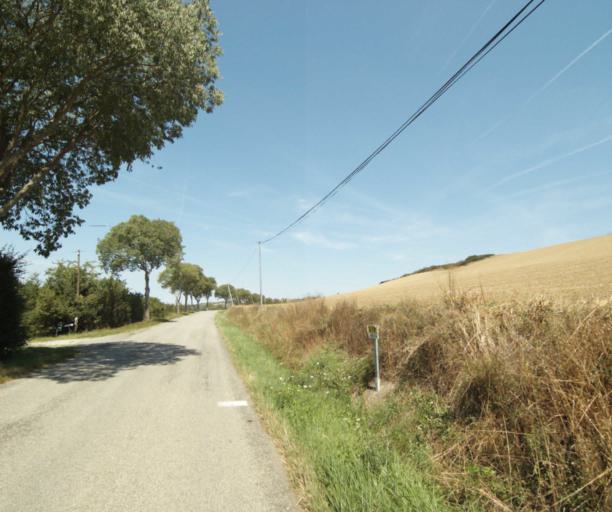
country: FR
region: Midi-Pyrenees
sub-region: Departement de l'Ariege
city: Lezat-sur-Leze
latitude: 43.2847
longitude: 1.3545
